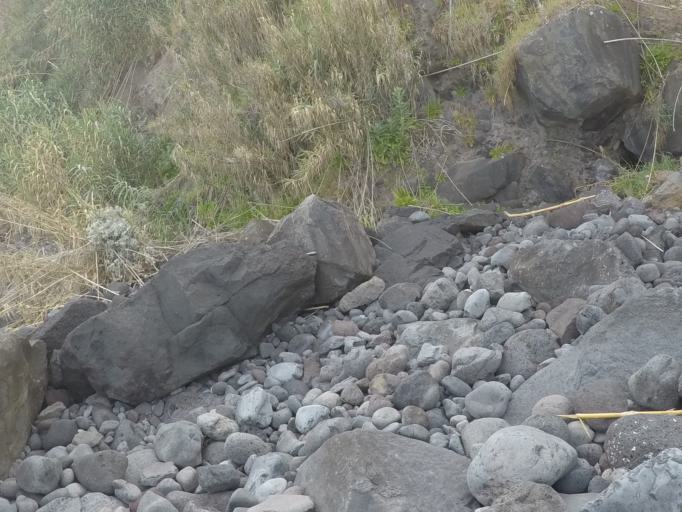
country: PT
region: Madeira
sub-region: Sao Vicente
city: Sao Vicente
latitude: 32.8251
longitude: -16.9976
